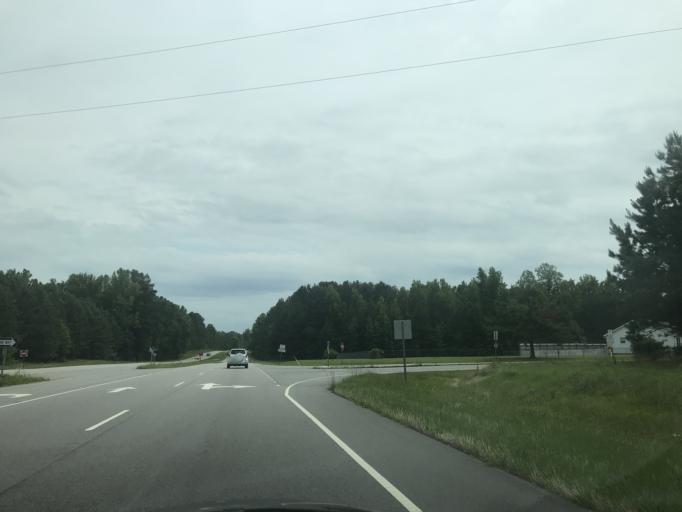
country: US
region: North Carolina
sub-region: Franklin County
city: Franklinton
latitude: 36.2078
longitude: -78.4484
